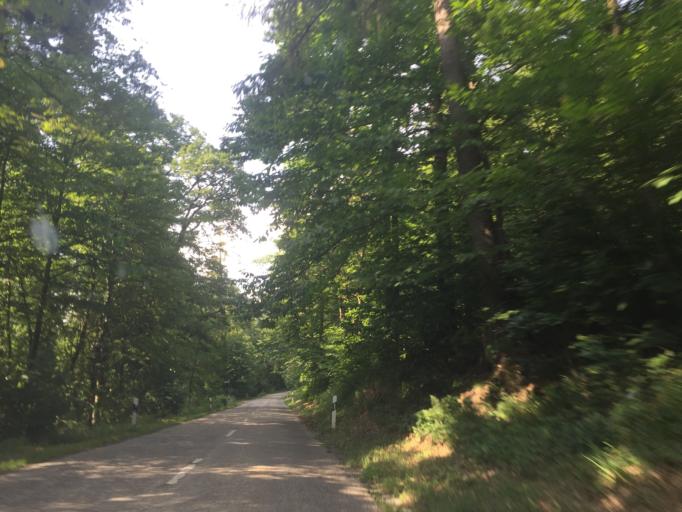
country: DE
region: Baden-Wuerttemberg
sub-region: Karlsruhe Region
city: Heidelberg
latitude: 49.3964
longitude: 8.7137
